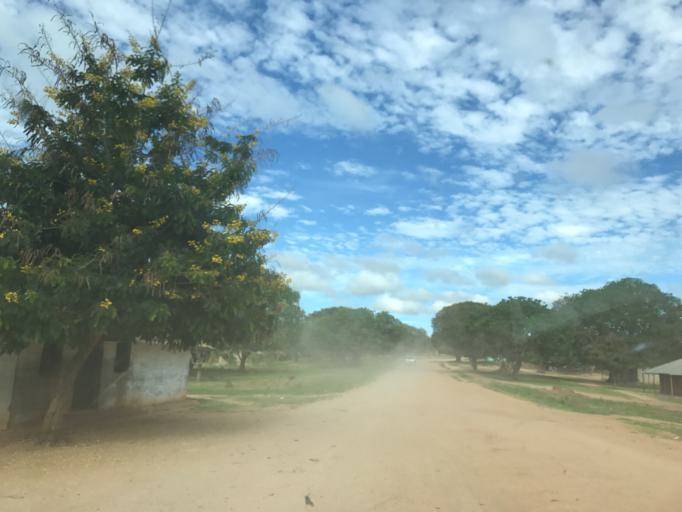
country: MZ
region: Nampula
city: Nacala
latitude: -14.4974
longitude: 40.5622
